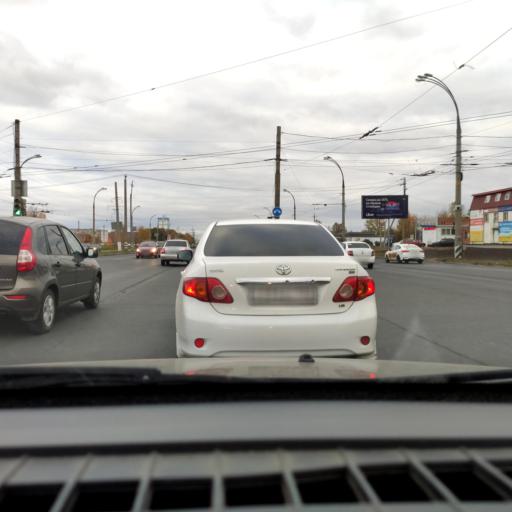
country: RU
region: Samara
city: Tol'yatti
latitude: 53.5392
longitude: 49.2637
